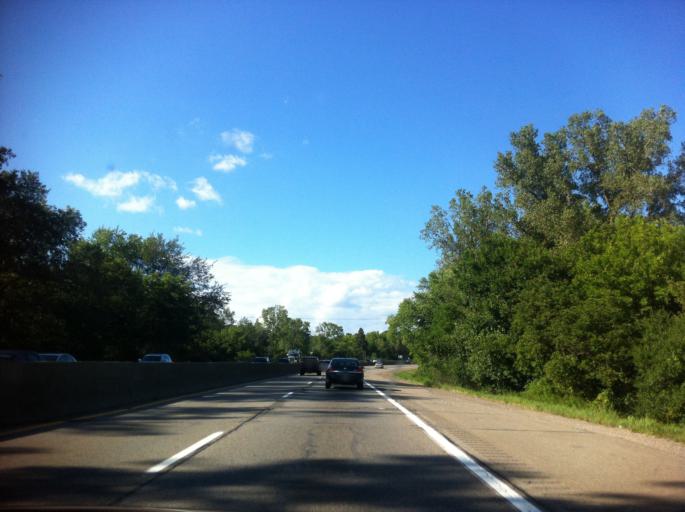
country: US
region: Michigan
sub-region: Washtenaw County
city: Ann Arbor
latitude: 42.3048
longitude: -83.7440
